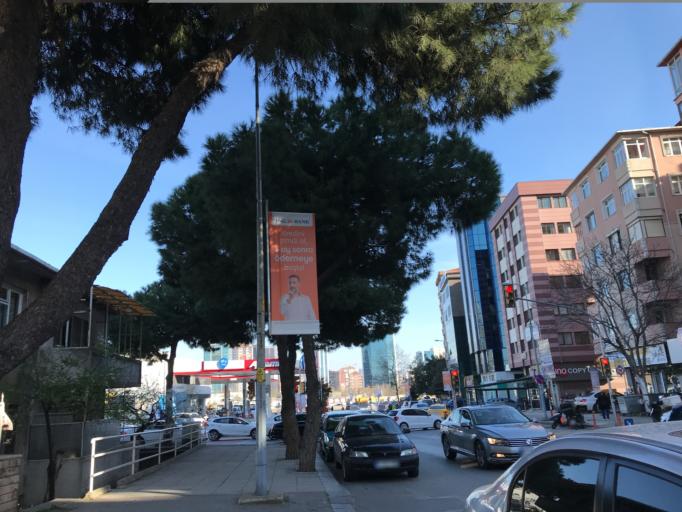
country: TR
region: Istanbul
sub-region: Atasehir
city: Atasehir
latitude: 40.9778
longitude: 29.0961
